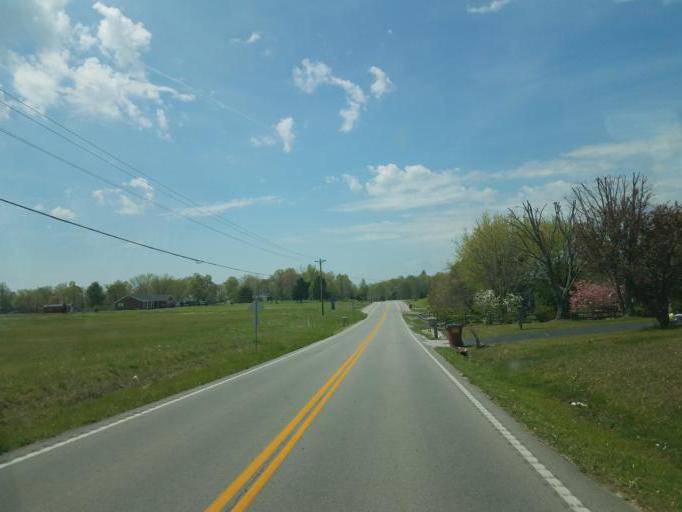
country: US
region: Kentucky
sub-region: Warren County
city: Bowling Green
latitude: 37.0947
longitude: -86.4409
